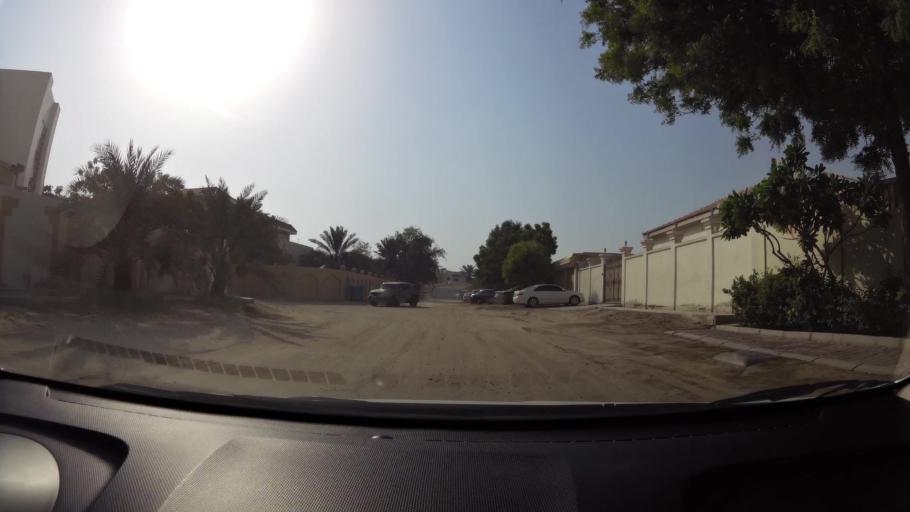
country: AE
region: Ajman
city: Ajman
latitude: 25.3802
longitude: 55.4205
